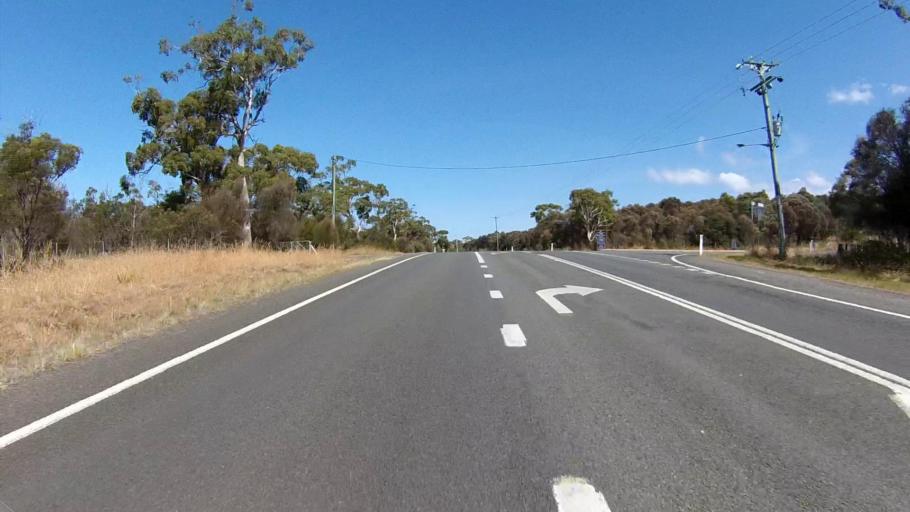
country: AU
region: Tasmania
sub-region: Sorell
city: Sorell
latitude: -42.1426
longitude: 148.0689
